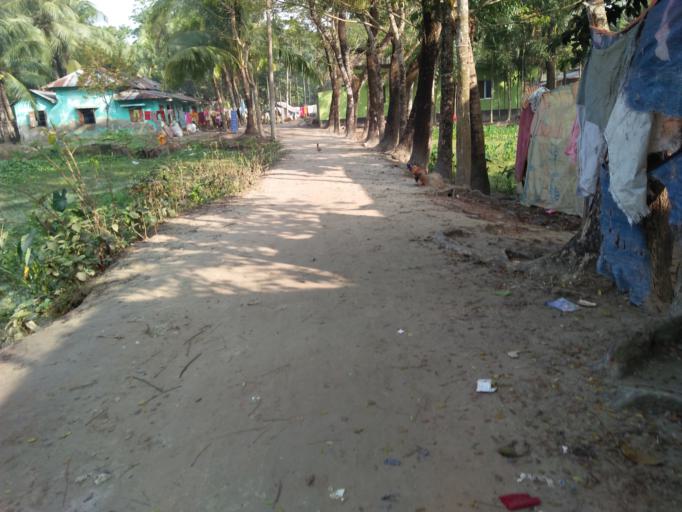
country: BD
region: Barisal
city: Bhola
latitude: 22.6782
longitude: 90.6401
